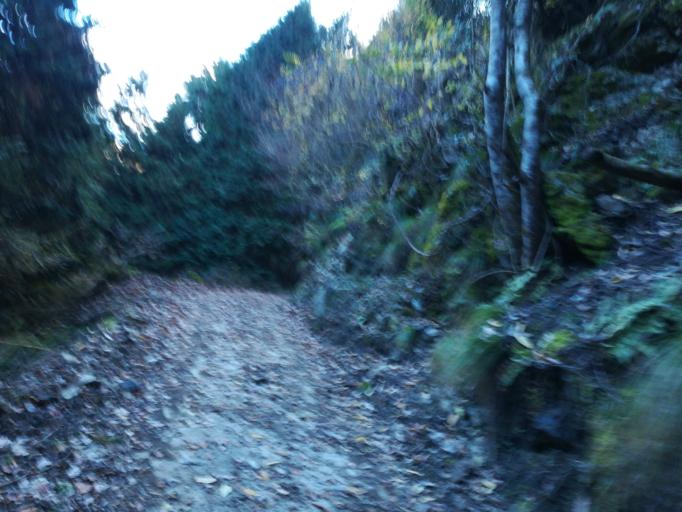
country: JP
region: Kyoto
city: Kameoka
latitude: 34.9839
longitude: 135.6272
